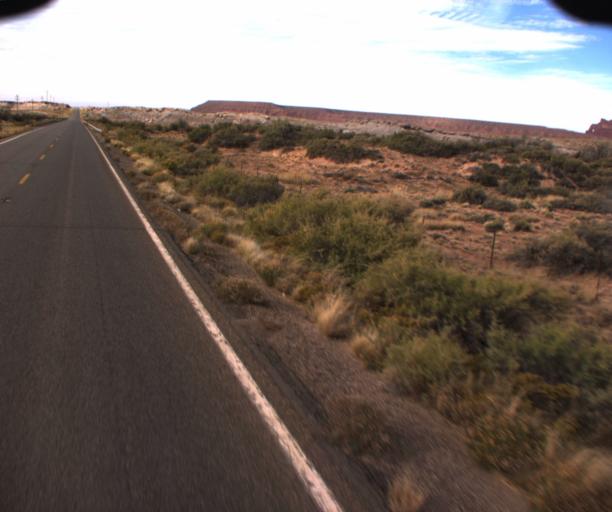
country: US
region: Arizona
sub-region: Apache County
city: Many Farms
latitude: 36.4950
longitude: -109.4908
